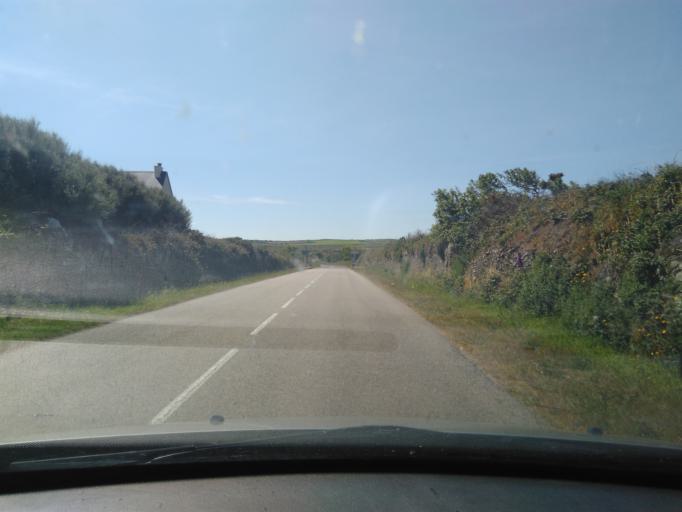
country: FR
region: Lower Normandy
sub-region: Departement de la Manche
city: Beaumont-Hague
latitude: 49.7075
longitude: -1.9318
